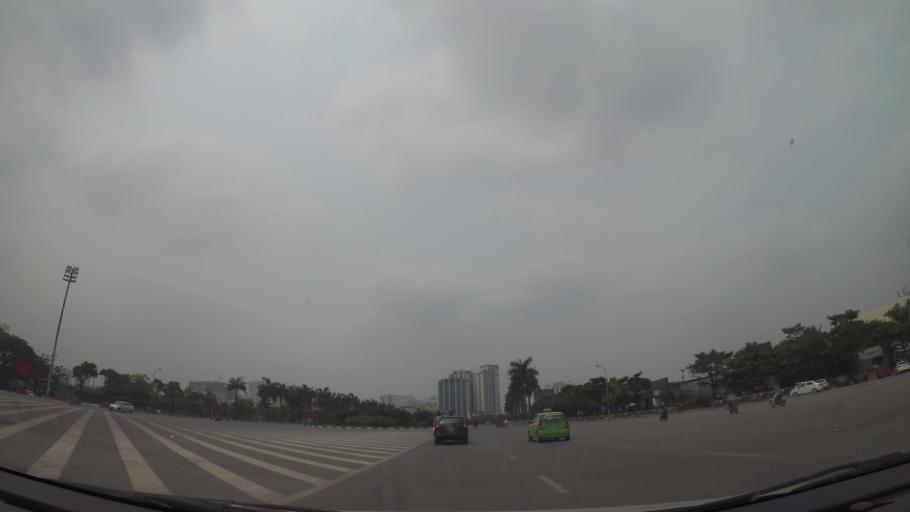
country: VN
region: Ha Noi
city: Cau Dien
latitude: 21.0214
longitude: 105.7667
